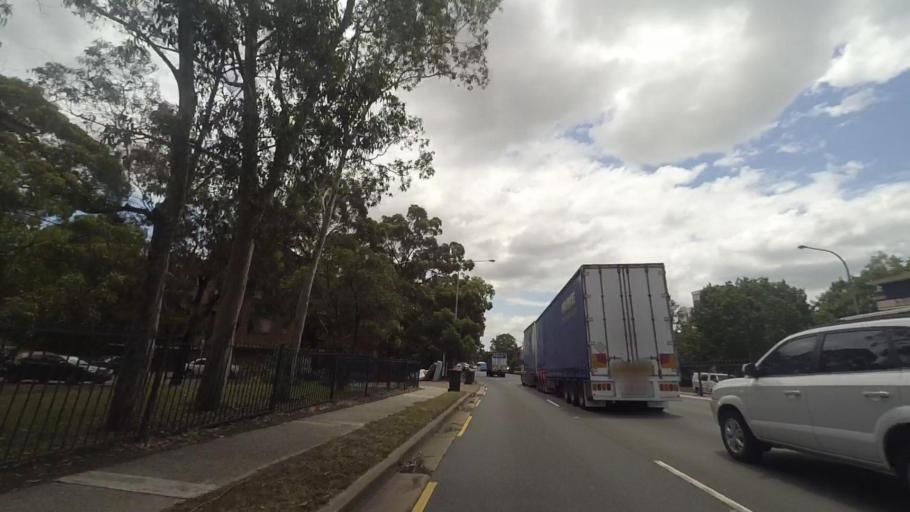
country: AU
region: New South Wales
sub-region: Fairfield
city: Liverpool
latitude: -33.9234
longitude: 150.9185
